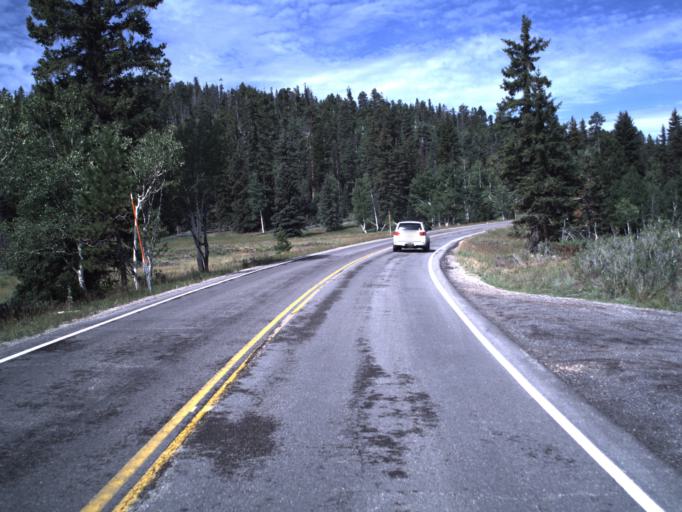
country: US
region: Utah
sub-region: Iron County
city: Parowan
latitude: 37.5139
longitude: -112.6869
